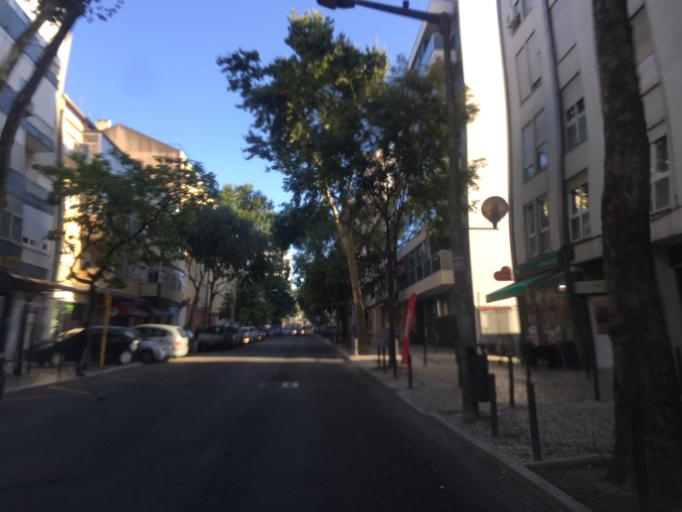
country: PT
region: Lisbon
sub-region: Odivelas
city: Pontinha
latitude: 38.7475
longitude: -9.1978
